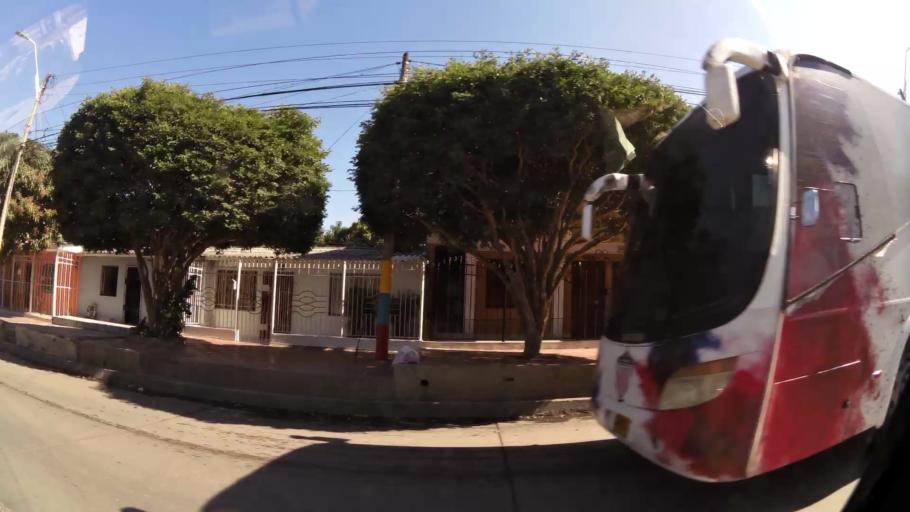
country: CO
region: Atlantico
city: Soledad
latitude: 10.9301
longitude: -74.8039
